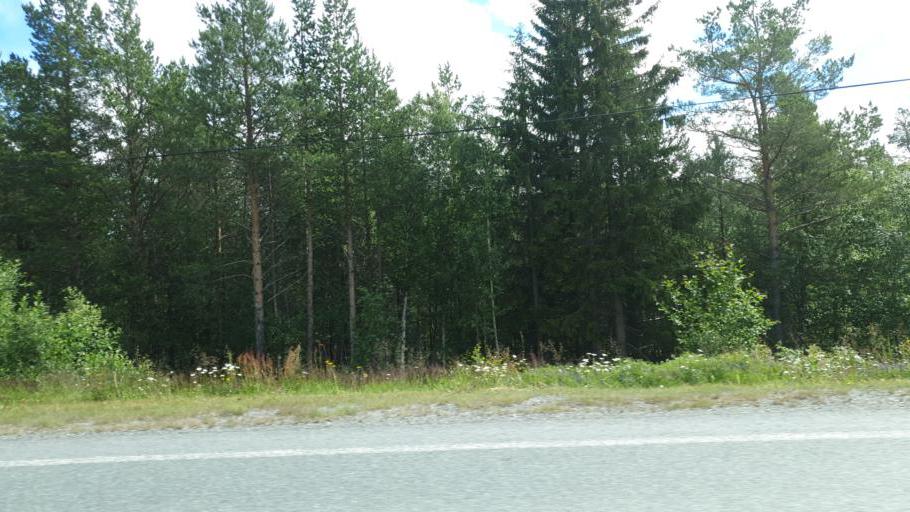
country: NO
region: Sor-Trondelag
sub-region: Rennebu
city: Berkak
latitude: 62.6778
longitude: 9.9200
